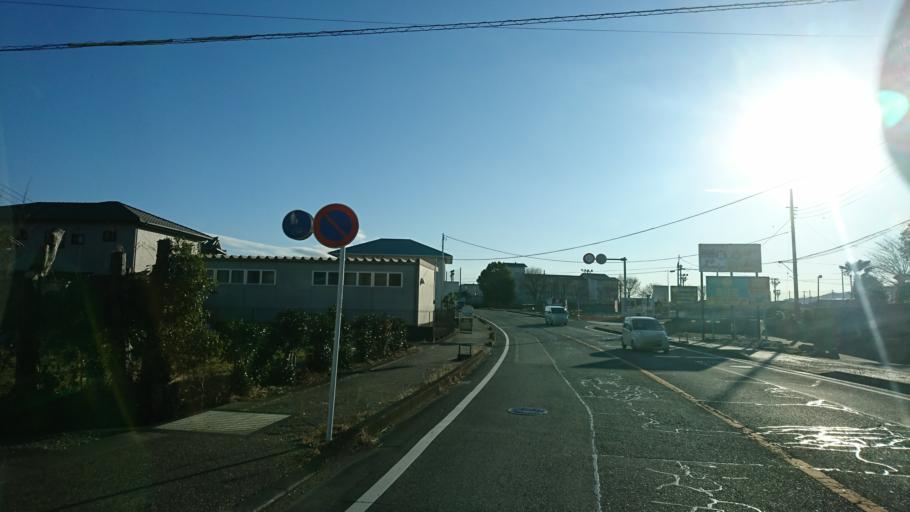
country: JP
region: Shizuoka
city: Fuji
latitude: 35.1699
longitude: 138.6540
